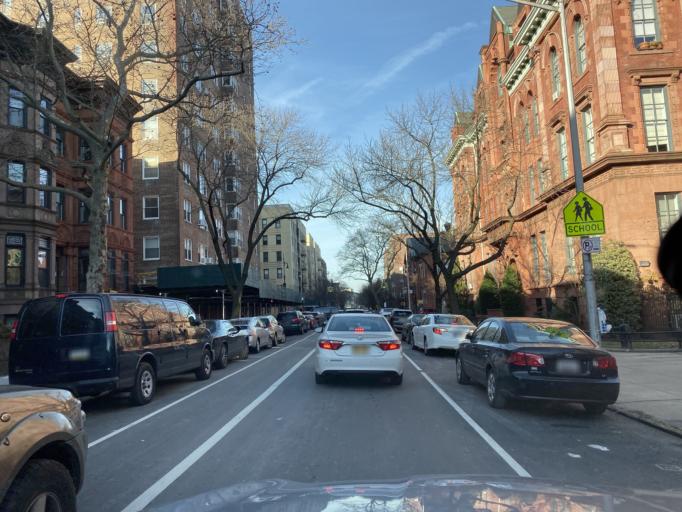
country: US
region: New York
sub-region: Kings County
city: Brooklyn
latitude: 40.6757
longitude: -73.9686
